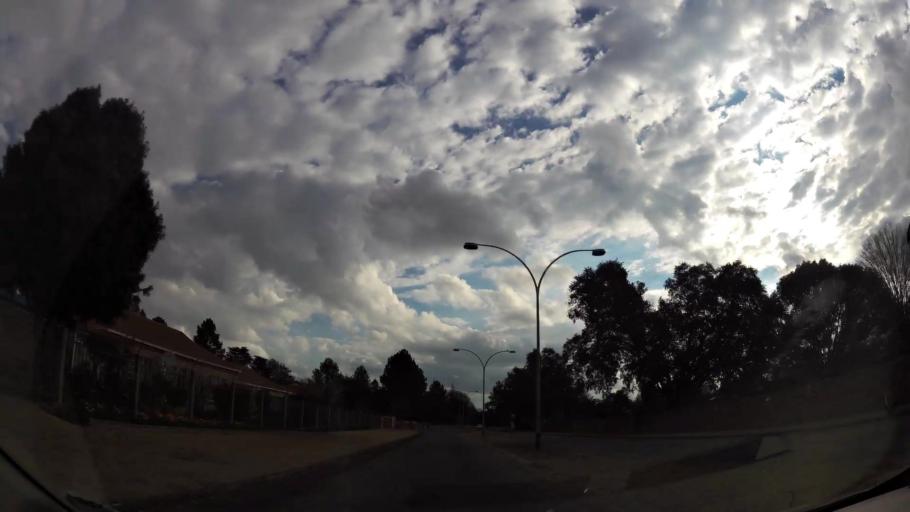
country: ZA
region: Orange Free State
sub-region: Fezile Dabi District Municipality
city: Sasolburg
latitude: -26.8030
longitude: 27.8283
